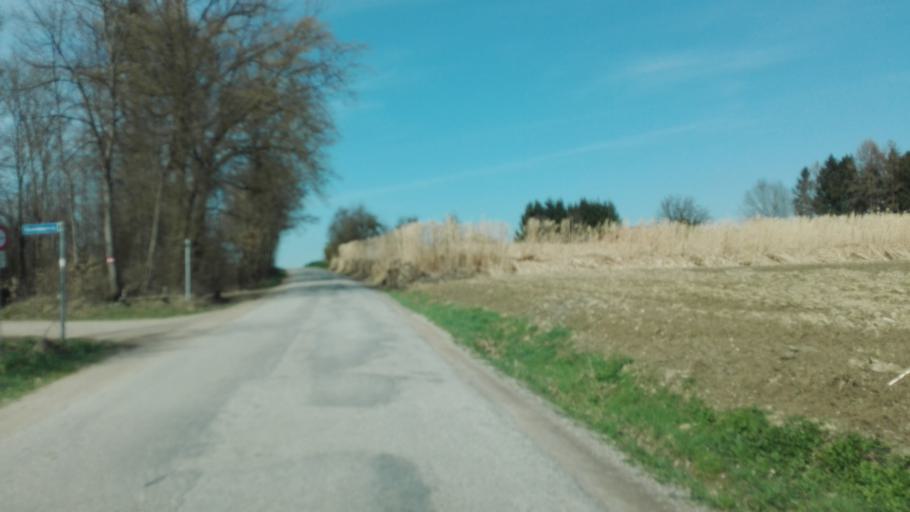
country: AT
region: Lower Austria
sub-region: Politischer Bezirk Amstetten
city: Ennsdorf
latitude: 48.2532
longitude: 14.5199
